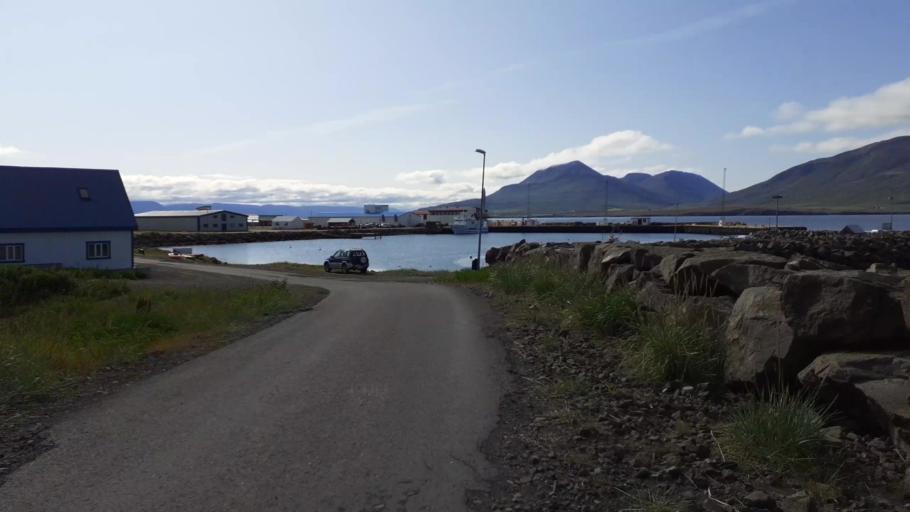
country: IS
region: Northeast
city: Dalvik
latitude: 65.9812
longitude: -18.3824
